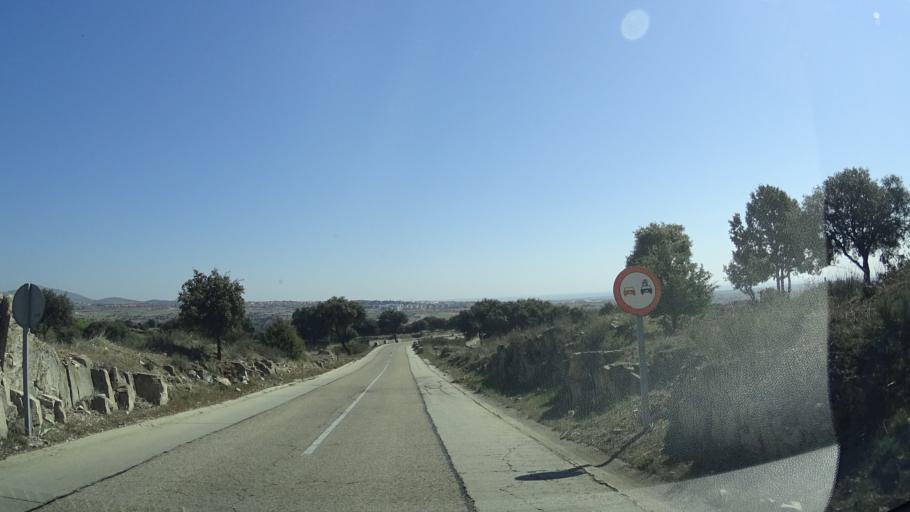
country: ES
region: Madrid
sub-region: Provincia de Madrid
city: Colmenar Viejo
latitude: 40.6458
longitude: -3.8255
